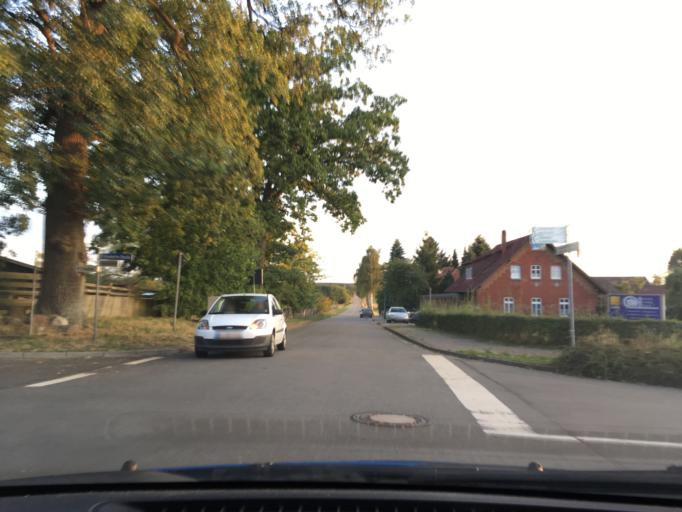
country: DE
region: Lower Saxony
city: Nahrendorf
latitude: 53.1734
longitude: 10.8134
